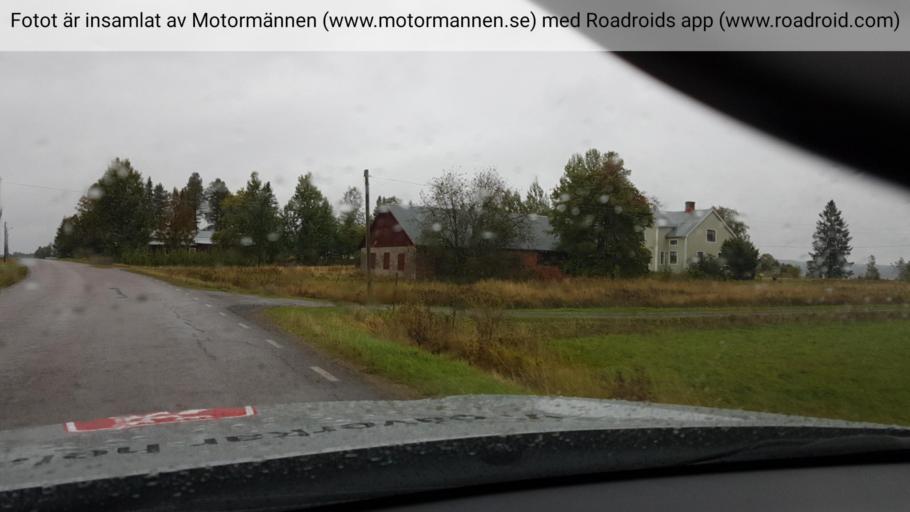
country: SE
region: Norrbotten
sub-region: Lulea Kommun
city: Gammelstad
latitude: 65.7609
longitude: 22.0960
